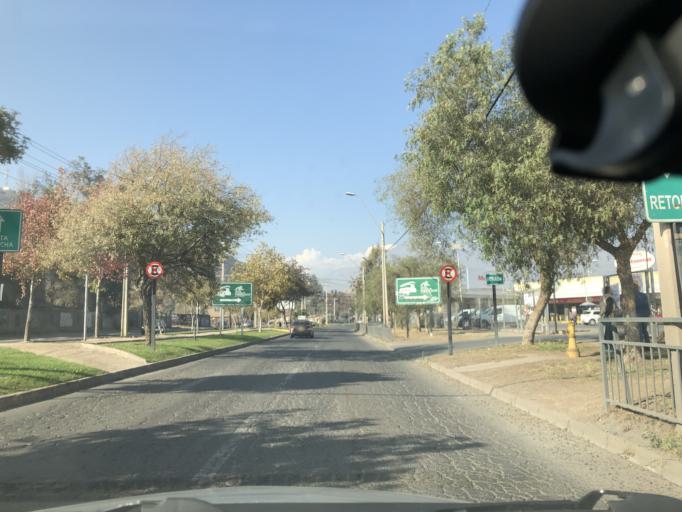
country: CL
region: Santiago Metropolitan
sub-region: Provincia de Cordillera
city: Puente Alto
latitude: -33.6101
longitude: -70.5520
